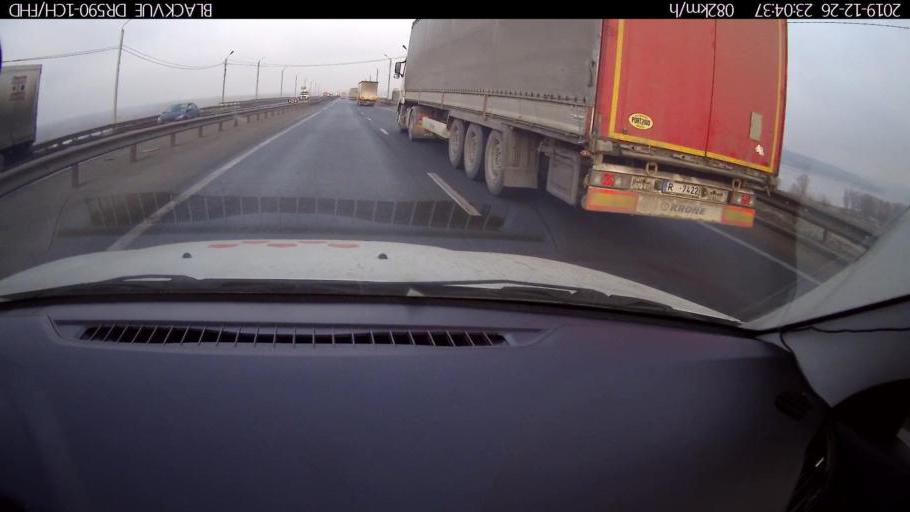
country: RU
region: Nizjnij Novgorod
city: Burevestnik
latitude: 56.1835
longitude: 43.7495
